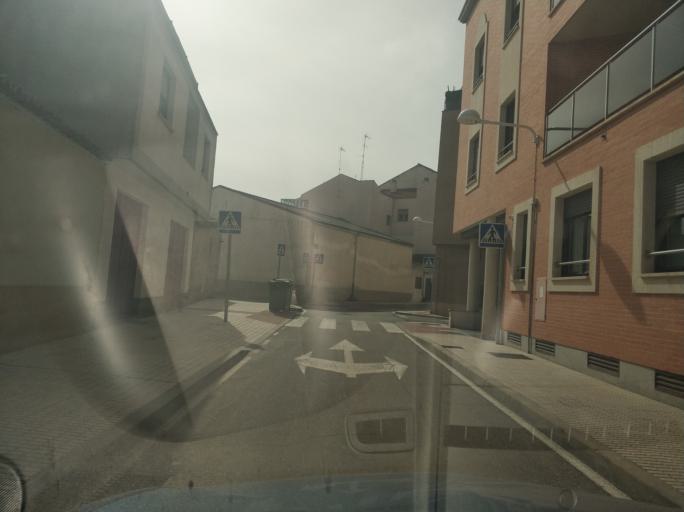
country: ES
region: Castille and Leon
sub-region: Provincia de Salamanca
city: Castellanos de Moriscos
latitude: 41.0202
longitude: -5.5915
